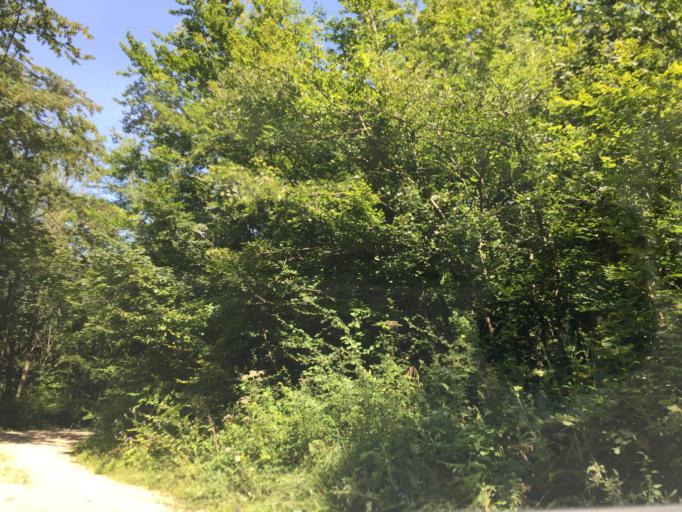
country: SI
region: Trbovlje
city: Trbovlje
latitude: 46.1484
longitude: 15.0327
